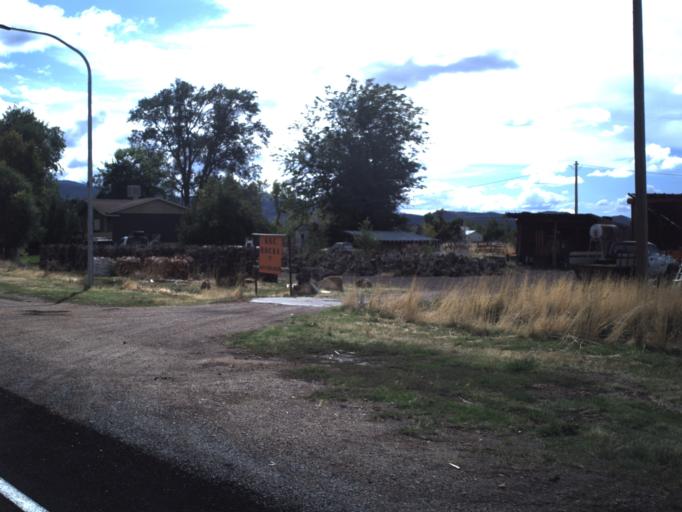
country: US
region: Utah
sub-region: Millard County
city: Fillmore
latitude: 38.8074
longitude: -112.4378
